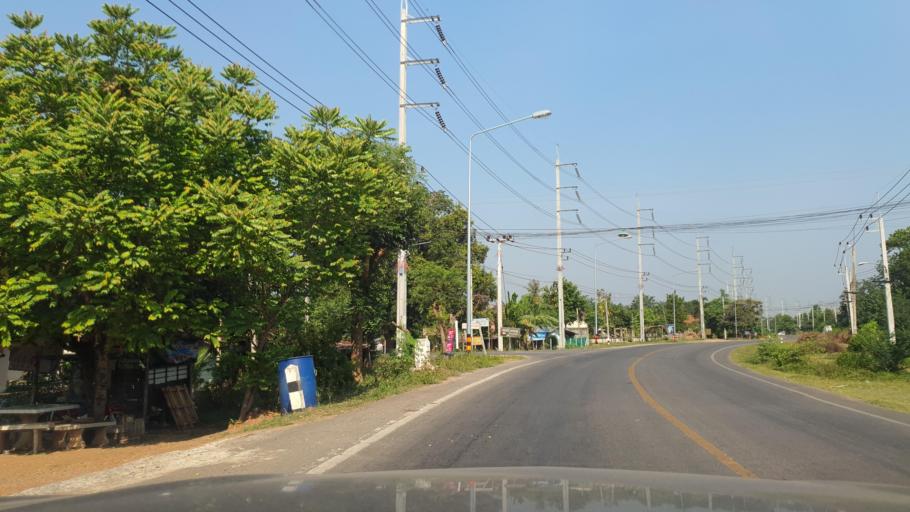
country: TH
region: Kanchanaburi
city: Kanchanaburi
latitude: 14.0373
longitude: 99.4786
